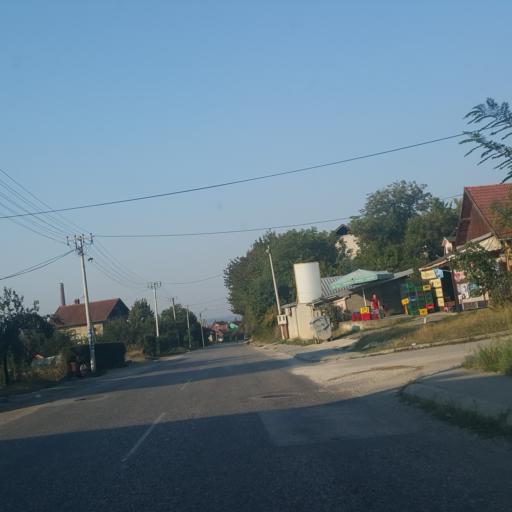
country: RS
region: Central Serbia
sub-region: Zajecarski Okrug
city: Zajecar
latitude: 43.9162
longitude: 22.2863
